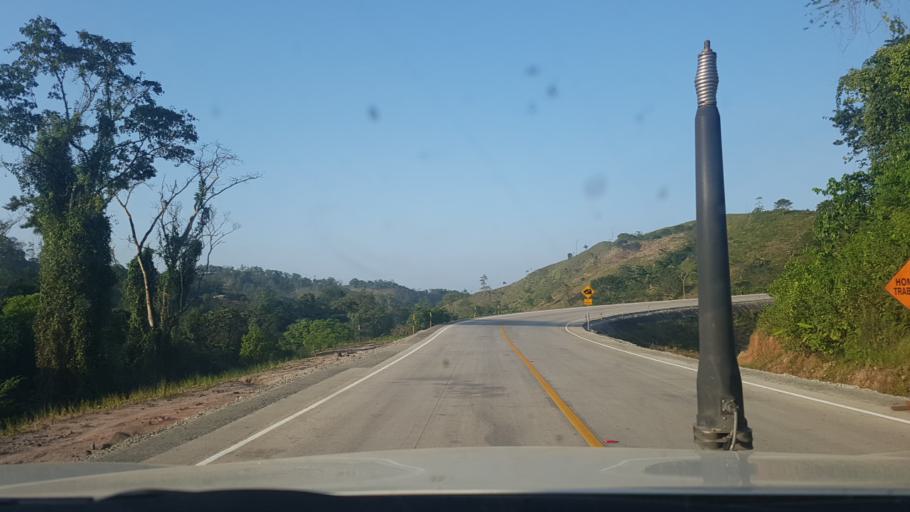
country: NI
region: Atlantico Sur
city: Rama
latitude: 11.8259
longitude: -84.0847
